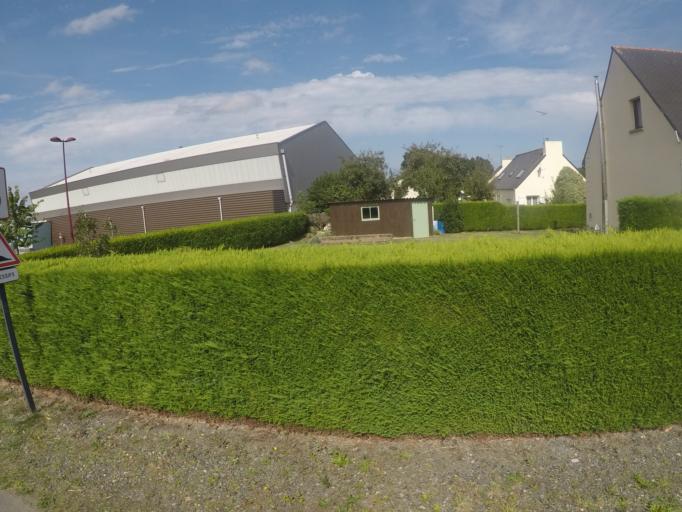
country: FR
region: Brittany
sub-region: Departement des Cotes-d'Armor
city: Goudelin
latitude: 48.6035
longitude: -3.0147
